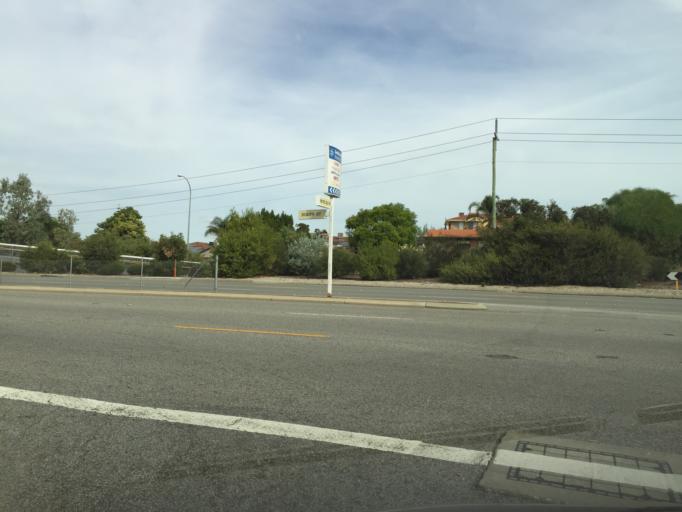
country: AU
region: Western Australia
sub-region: Canning
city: Willetton
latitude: -32.0668
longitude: 115.8784
